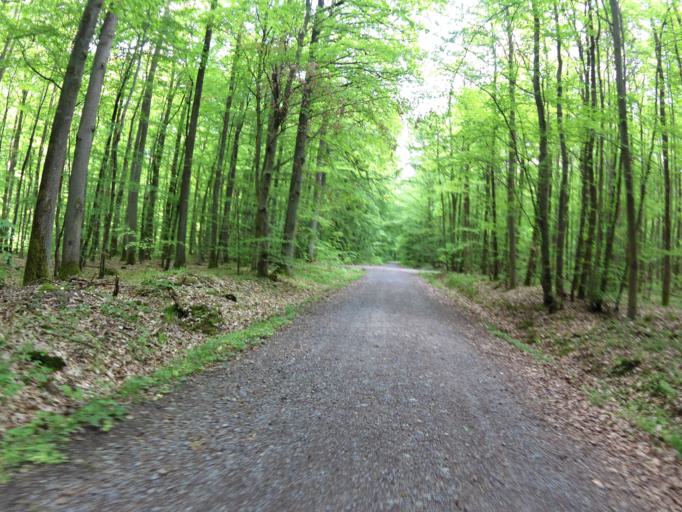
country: DE
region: Bavaria
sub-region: Regierungsbezirk Unterfranken
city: Kist
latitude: 49.7398
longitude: 9.8562
